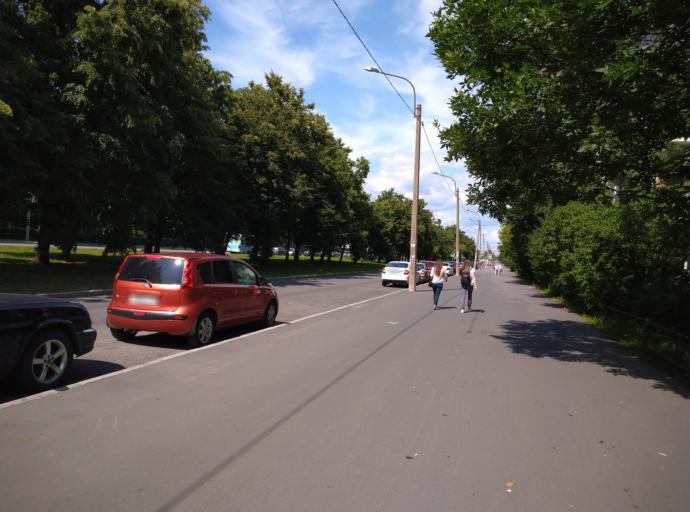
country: RU
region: St.-Petersburg
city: Kupchino
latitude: 59.8604
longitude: 30.3379
